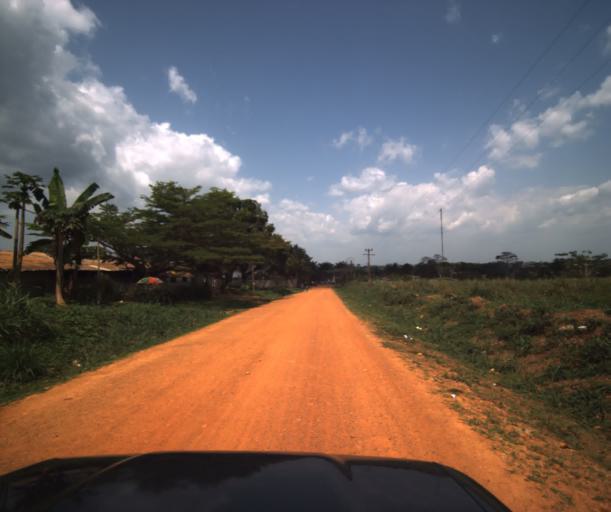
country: CM
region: Centre
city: Eseka
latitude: 3.5475
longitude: 11.0261
